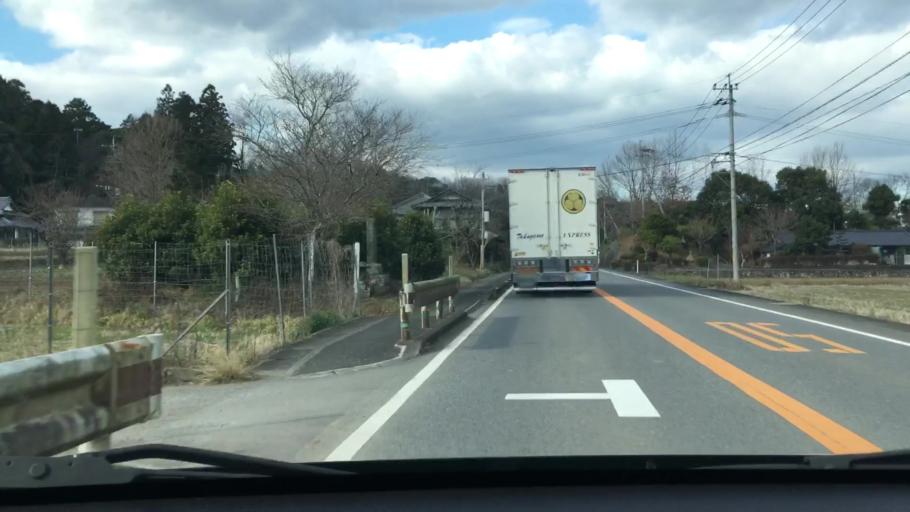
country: JP
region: Oita
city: Usuki
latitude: 33.0199
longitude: 131.6982
